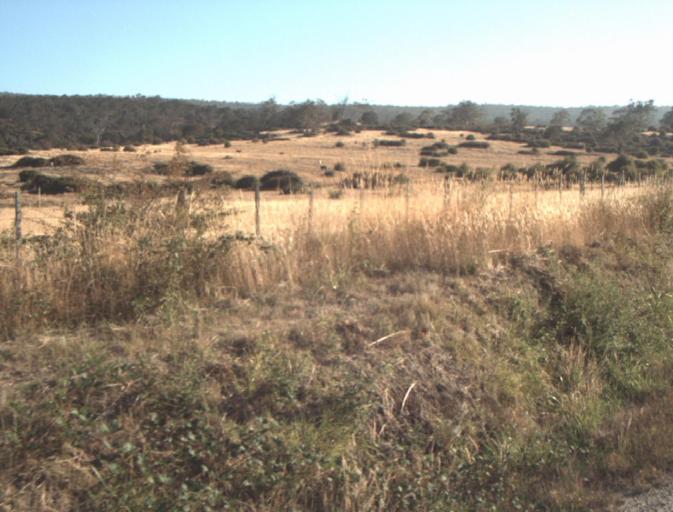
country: AU
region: Tasmania
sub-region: Launceston
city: Newstead
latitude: -41.4356
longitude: 147.2000
